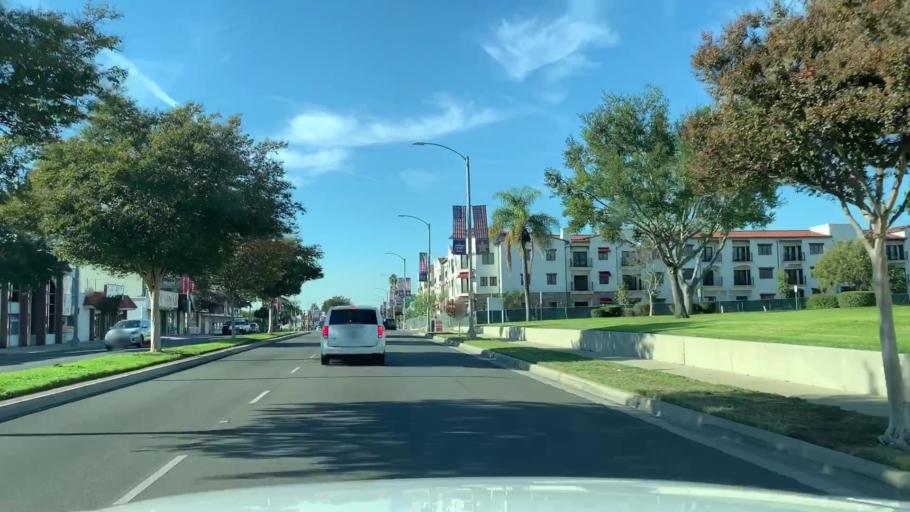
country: US
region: California
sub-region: Los Angeles County
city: South Whittier
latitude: 33.9543
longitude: -118.0169
